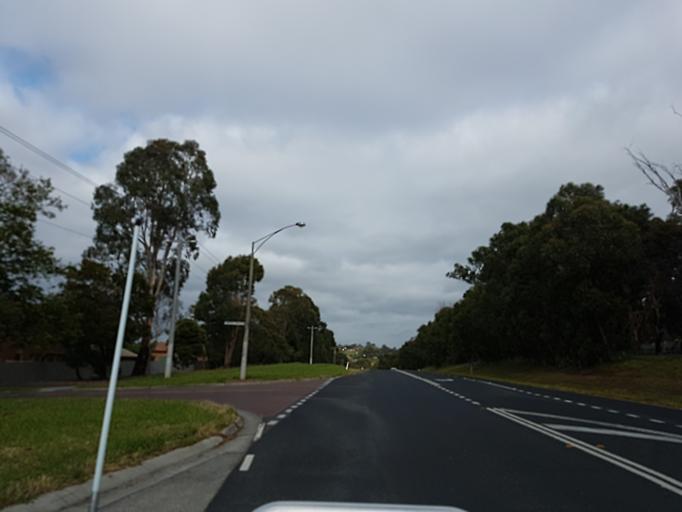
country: AU
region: Victoria
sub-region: Yarra Ranges
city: Lilydale
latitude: -37.7759
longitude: 145.3391
